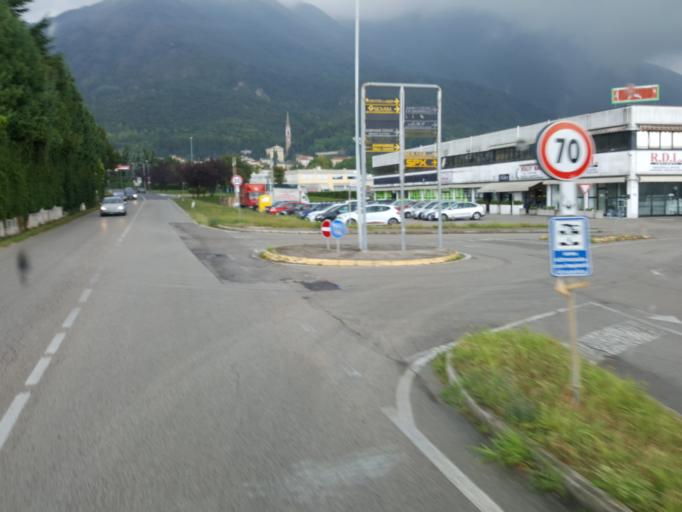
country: IT
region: Veneto
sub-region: Provincia di Vicenza
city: Santorso
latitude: 45.7289
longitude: 11.3877
